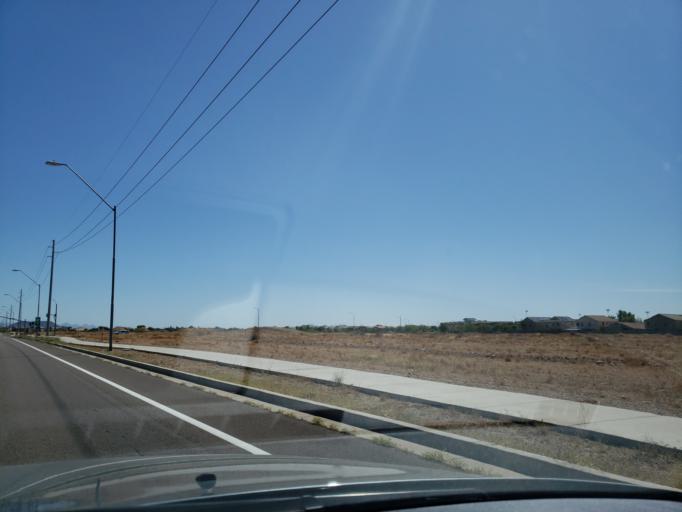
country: US
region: Arizona
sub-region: Maricopa County
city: Sun City West
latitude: 33.6815
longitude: -112.2725
